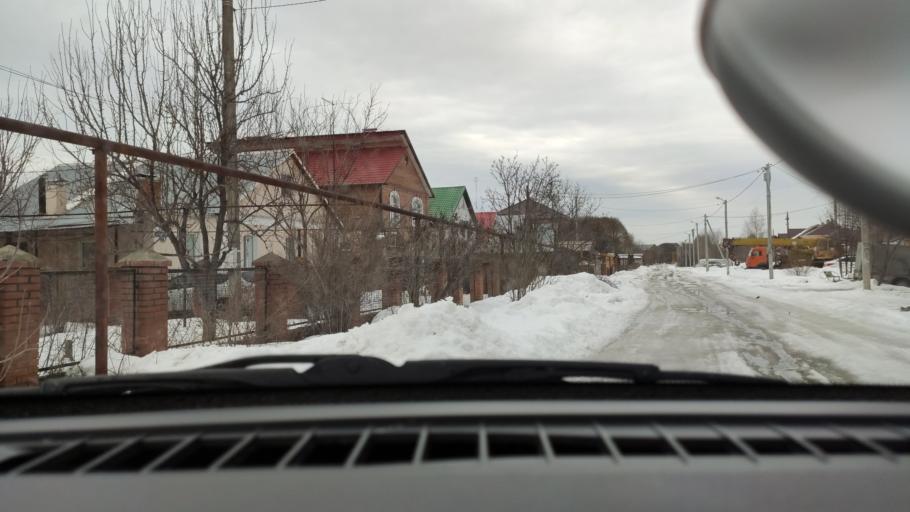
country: RU
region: Samara
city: Kurumoch
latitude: 53.4909
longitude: 50.0199
